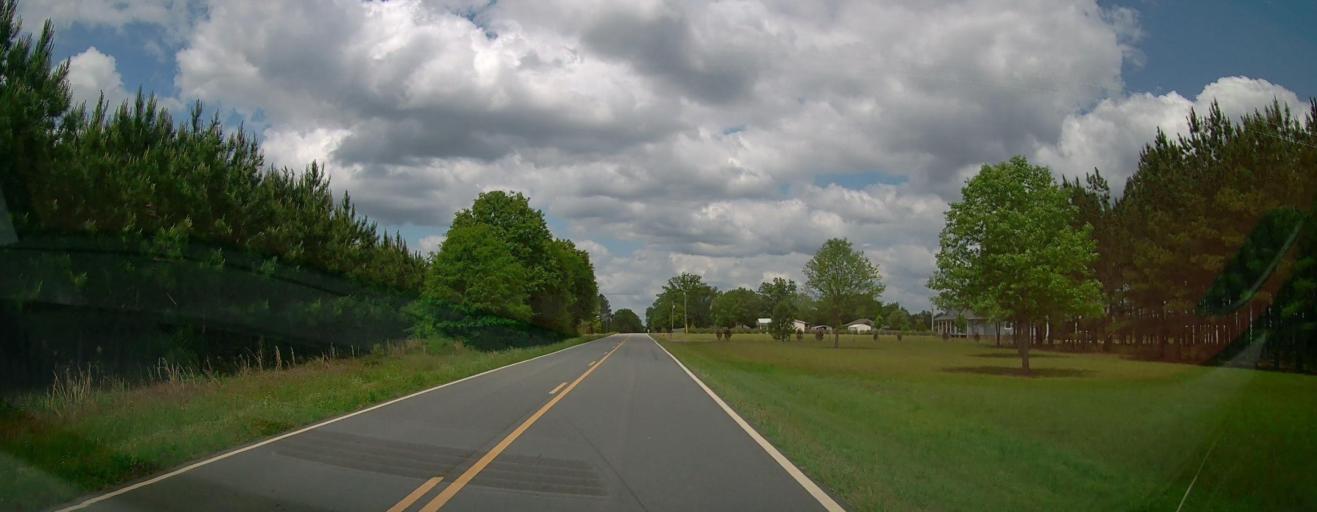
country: US
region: Georgia
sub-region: Laurens County
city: Dublin
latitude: 32.5962
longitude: -82.9530
